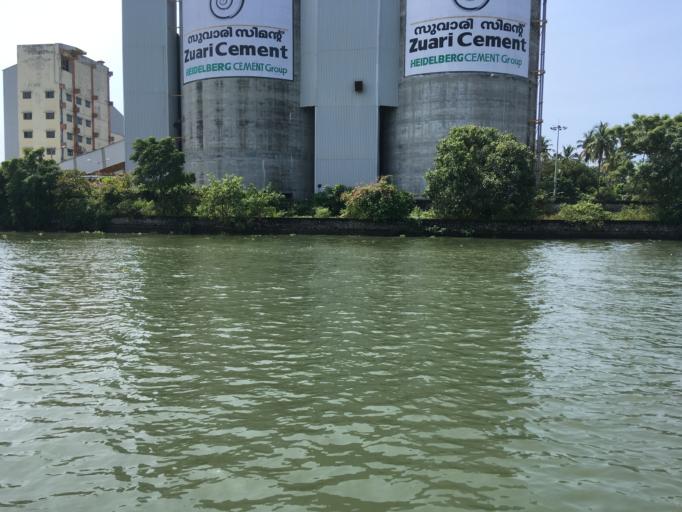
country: IN
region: Kerala
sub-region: Ernakulam
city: Cochin
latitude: 9.9699
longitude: 76.2636
